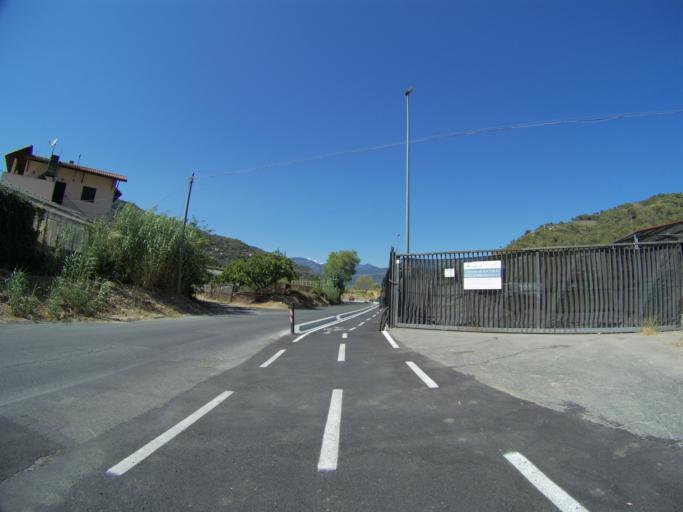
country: IT
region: Liguria
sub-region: Provincia di Imperia
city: Camporosso
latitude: 43.8186
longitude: 7.6327
